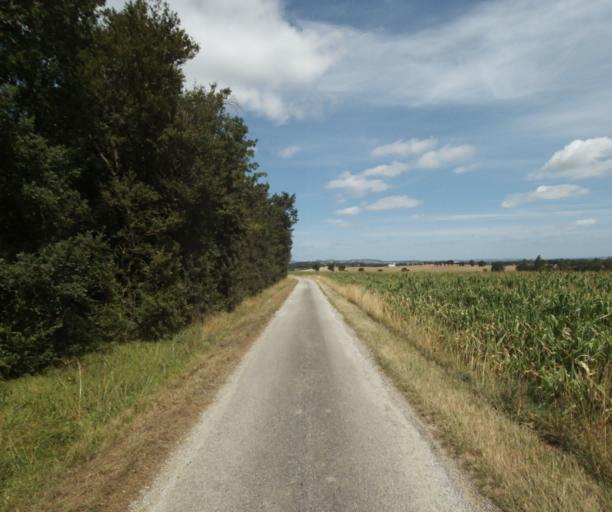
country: FR
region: Midi-Pyrenees
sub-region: Departement du Tarn
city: Dourgne
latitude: 43.4870
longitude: 2.1012
